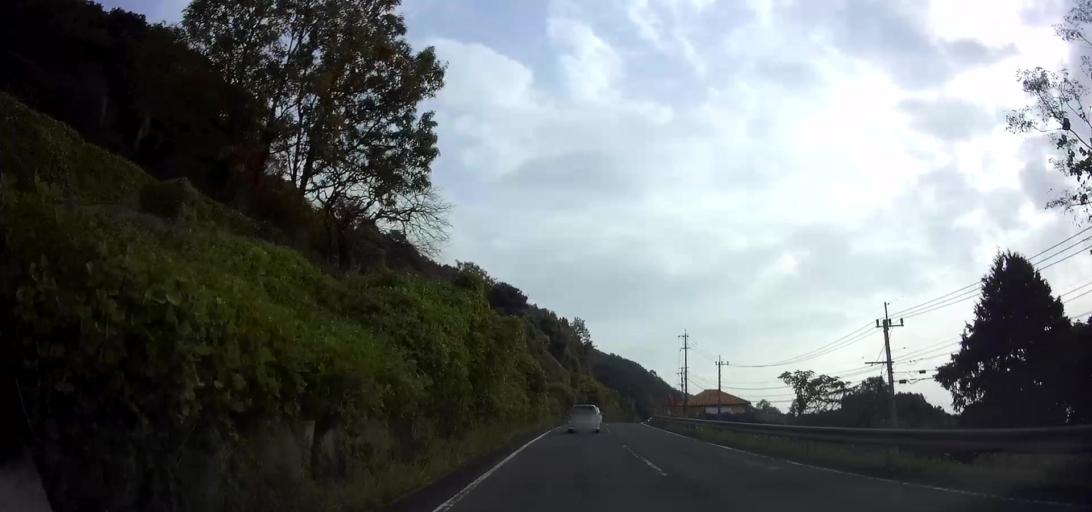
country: JP
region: Nagasaki
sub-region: Isahaya-shi
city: Isahaya
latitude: 32.7950
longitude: 130.1031
